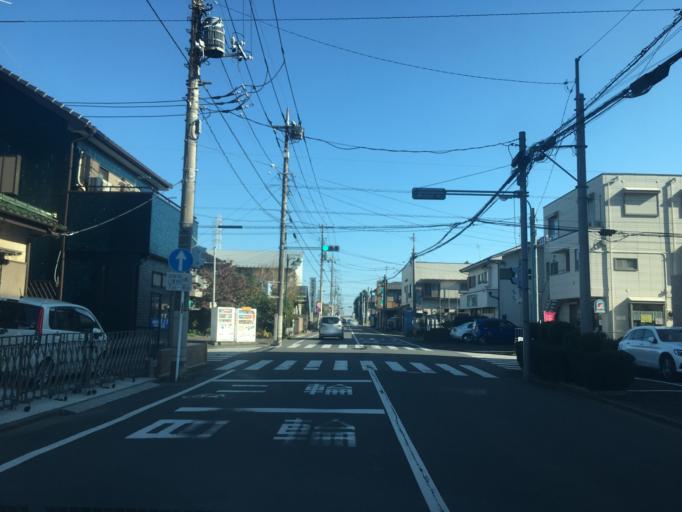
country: JP
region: Saitama
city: Kawagoe
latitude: 35.8965
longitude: 139.4754
